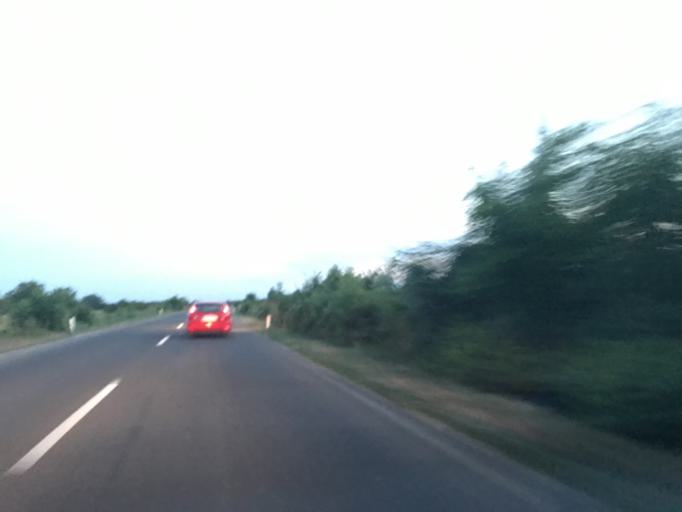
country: RS
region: Central Serbia
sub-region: Branicevski Okrug
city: Pozarevac
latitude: 44.6172
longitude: 21.1459
